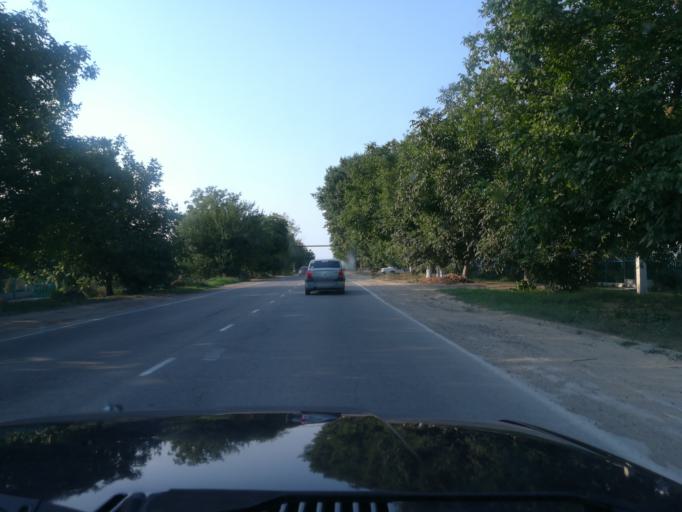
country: RU
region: Krasnodarskiy
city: Yurovka
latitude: 45.1160
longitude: 37.4220
